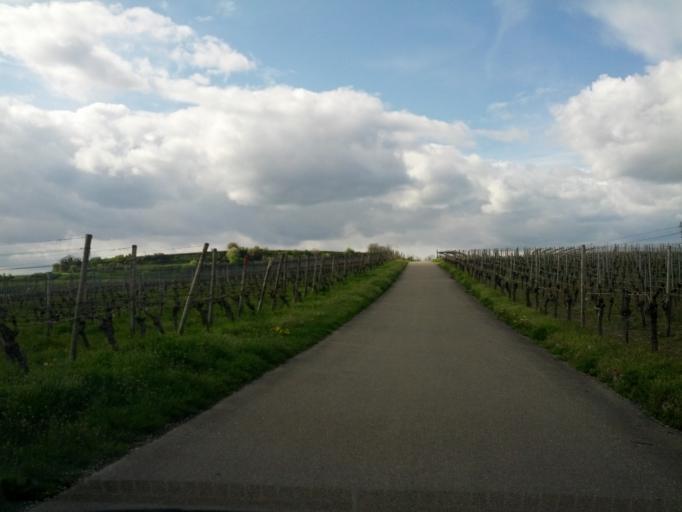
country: DE
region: Baden-Wuerttemberg
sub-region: Freiburg Region
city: Merdingen
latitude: 47.9682
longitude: 7.6878
